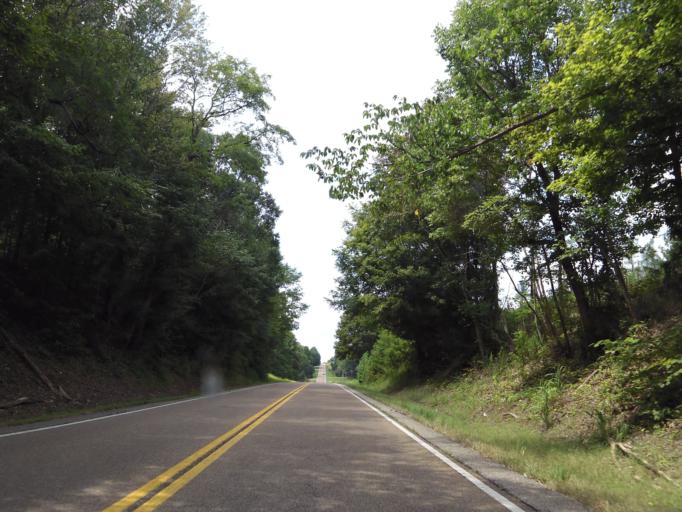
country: US
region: Tennessee
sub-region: Henderson County
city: Lexington
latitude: 35.5111
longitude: -88.3127
